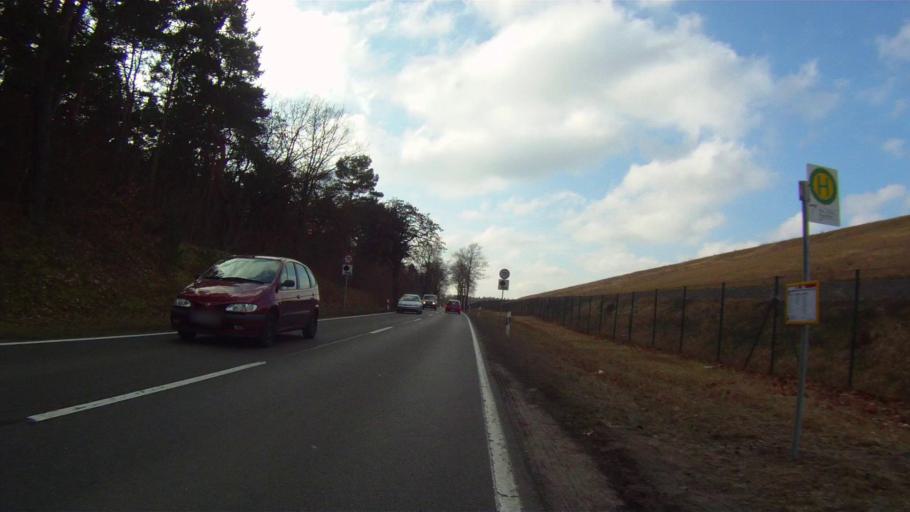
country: DE
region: Brandenburg
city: Erkner
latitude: 52.3851
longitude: 13.7291
